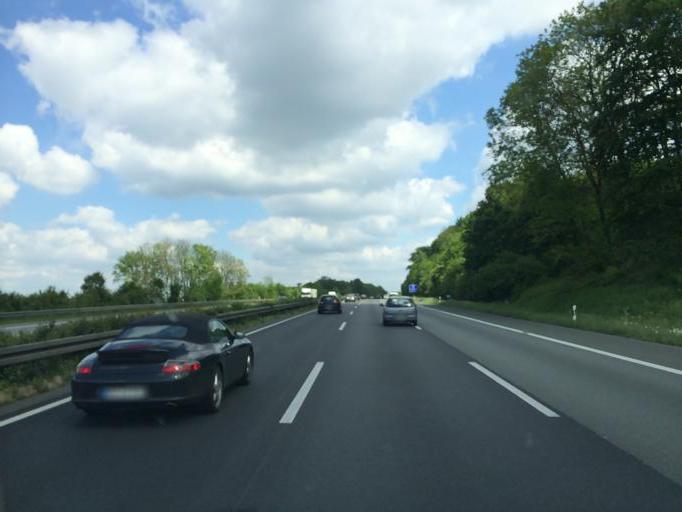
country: DE
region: North Rhine-Westphalia
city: Oelde
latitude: 51.8229
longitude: 8.1850
